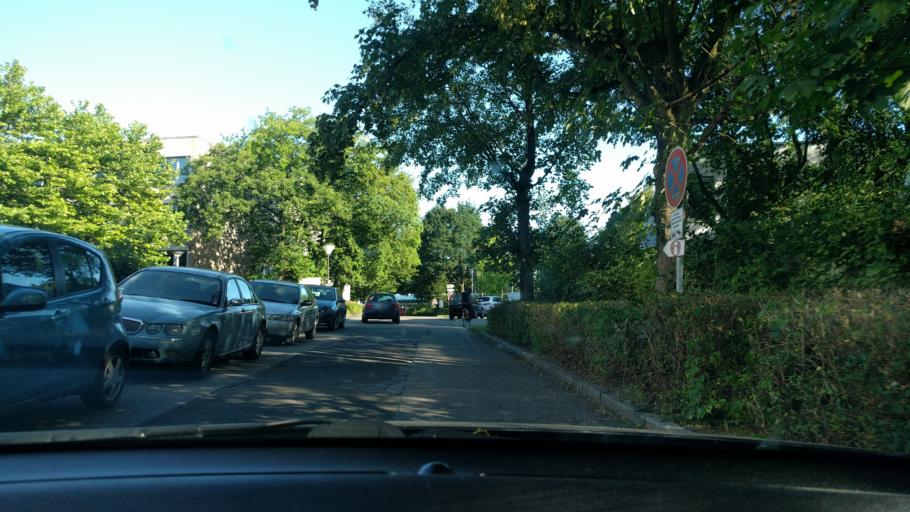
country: DE
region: North Rhine-Westphalia
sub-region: Regierungsbezirk Arnsberg
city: Dortmund
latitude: 51.4841
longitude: 7.4149
